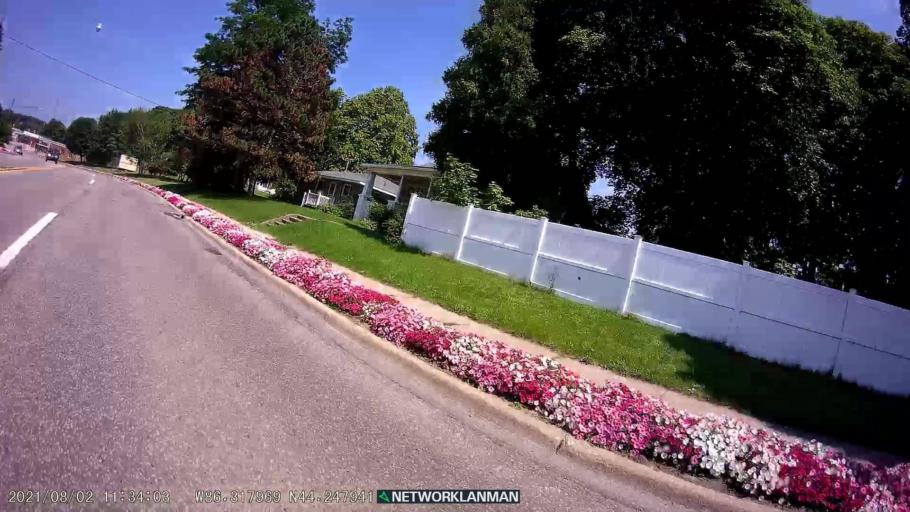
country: US
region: Michigan
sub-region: Manistee County
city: Manistee
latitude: 44.2481
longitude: -86.3179
